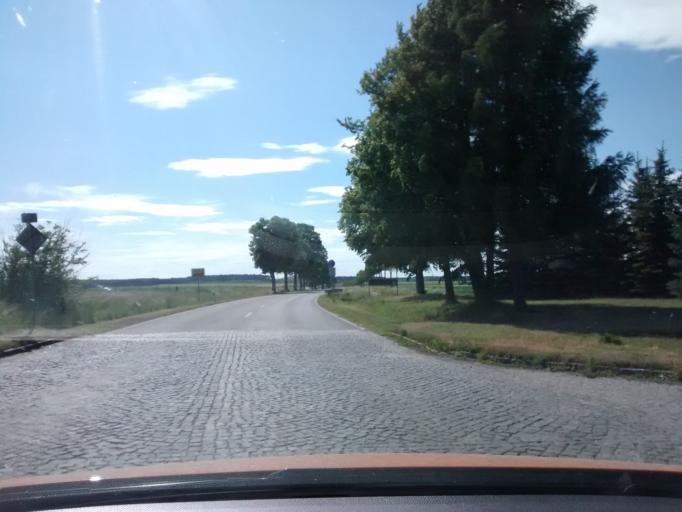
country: DE
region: Brandenburg
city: Juterbog
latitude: 51.9849
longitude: 13.1701
